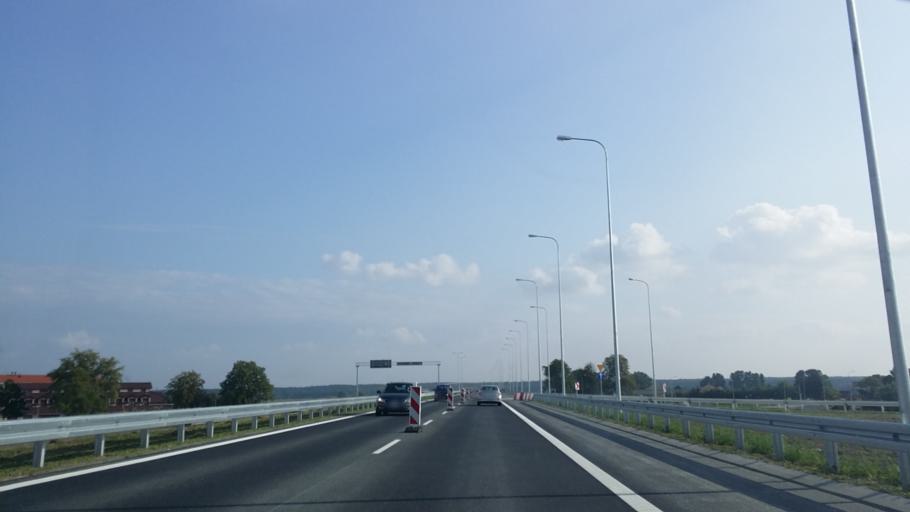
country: PL
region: Lubusz
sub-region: Powiat miedzyrzecki
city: Miedzyrzecz
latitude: 52.4439
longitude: 15.5590
